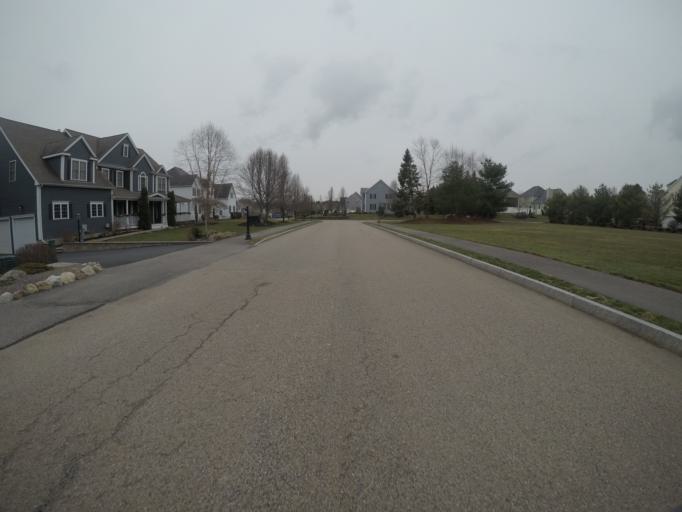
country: US
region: Massachusetts
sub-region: Bristol County
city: Easton
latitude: 42.0161
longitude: -71.1093
